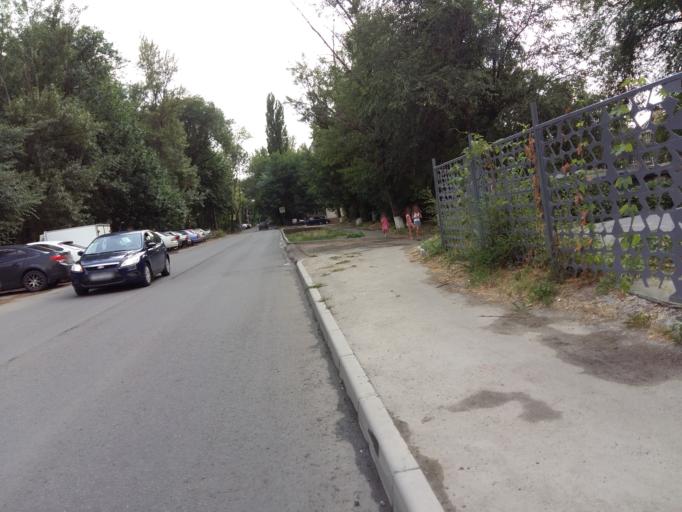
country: RU
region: Rostov
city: Imeni Chkalova
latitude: 47.2786
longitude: 39.7364
